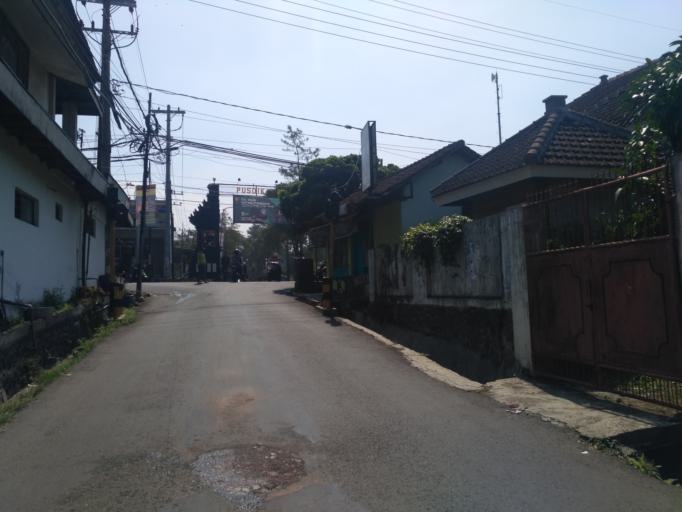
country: ID
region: East Java
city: Batu
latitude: -7.9024
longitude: 112.5811
